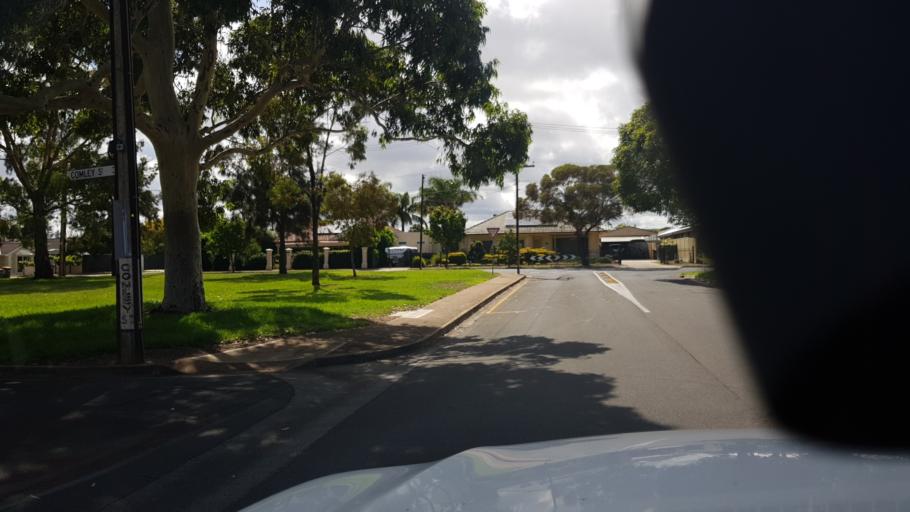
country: AU
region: South Australia
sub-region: Holdfast Bay
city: Seacliff Park
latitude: -35.0229
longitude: 138.5317
